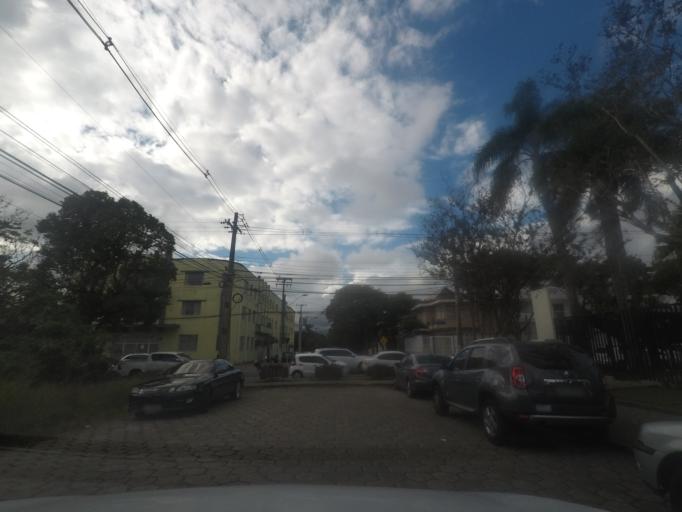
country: BR
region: Parana
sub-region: Curitiba
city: Curitiba
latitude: -25.4317
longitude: -49.2481
